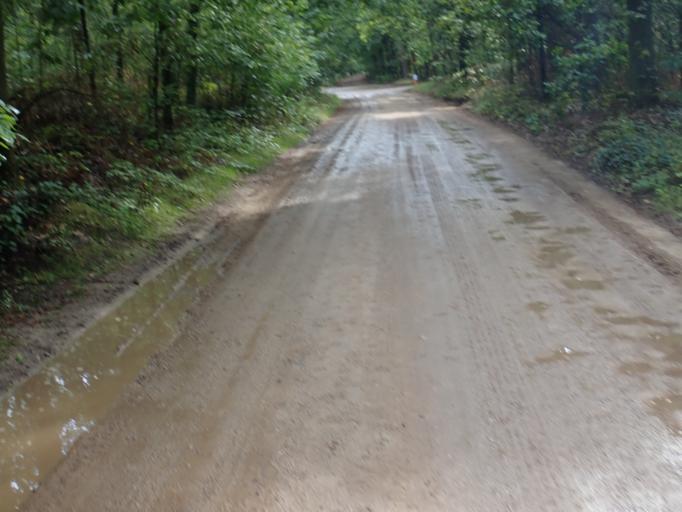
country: BE
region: Flanders
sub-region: Provincie Antwerpen
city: Lille
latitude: 51.2732
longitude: 4.8266
